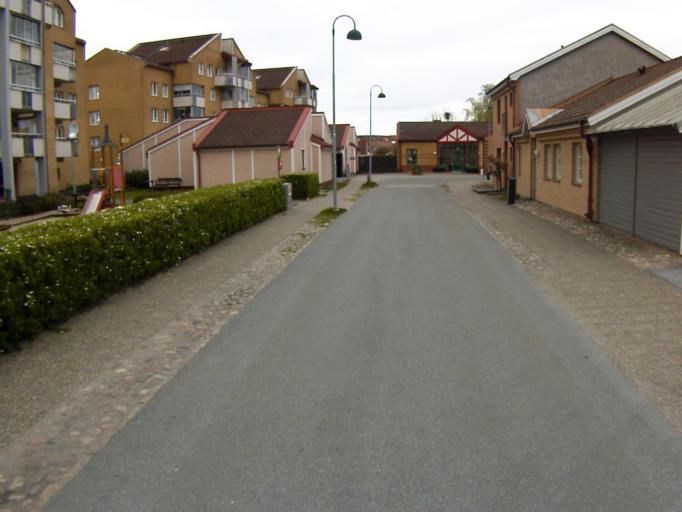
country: SE
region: Skane
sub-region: Kristianstads Kommun
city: Kristianstad
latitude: 56.0207
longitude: 14.1411
